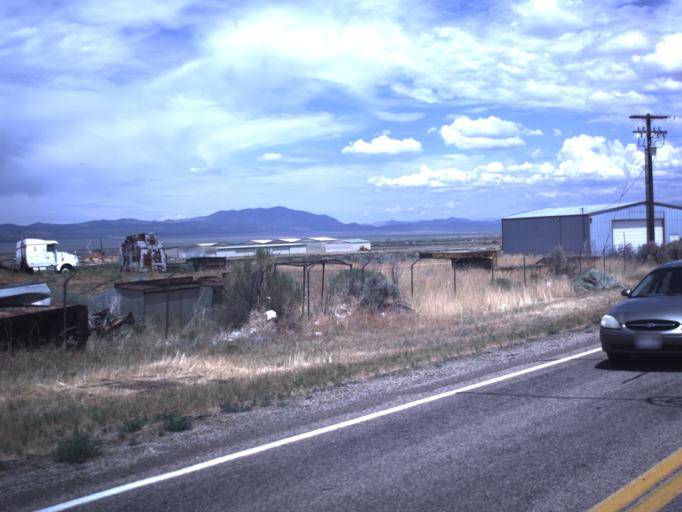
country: US
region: Utah
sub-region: Iron County
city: Parowan
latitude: 37.8546
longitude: -112.8214
